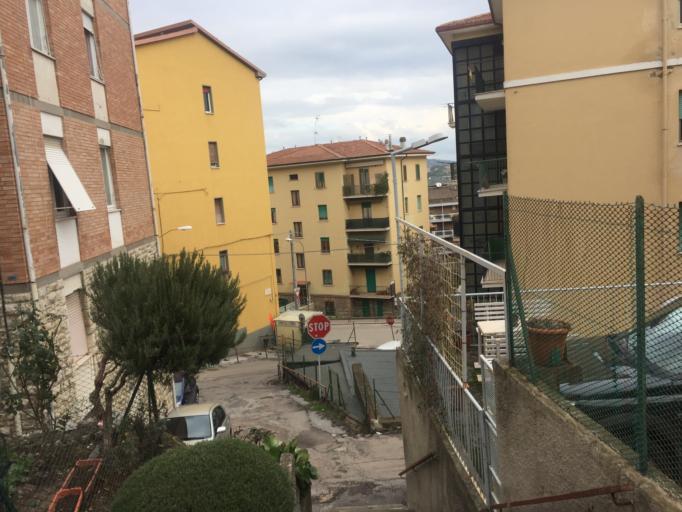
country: IT
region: Umbria
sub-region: Provincia di Perugia
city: Perugia
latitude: 43.1176
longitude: 12.4000
